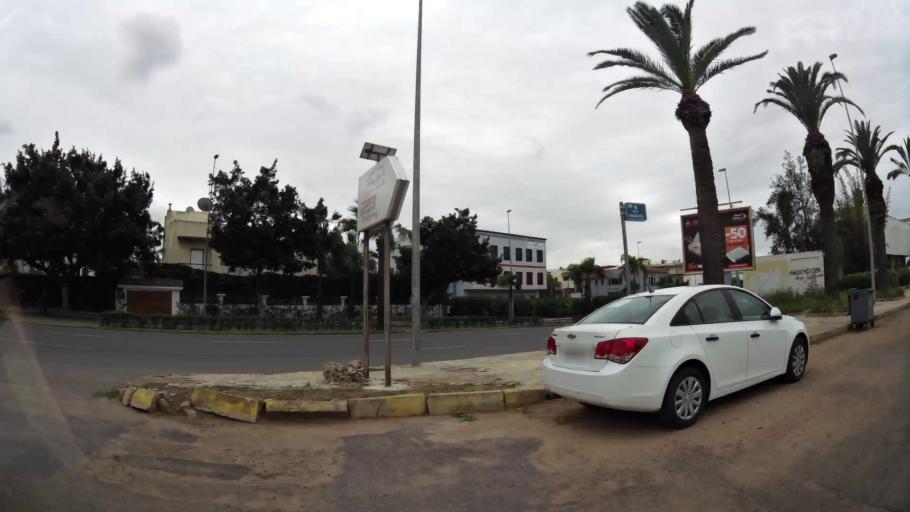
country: MA
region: Grand Casablanca
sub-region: Casablanca
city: Casablanca
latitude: 33.5620
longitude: -7.6229
